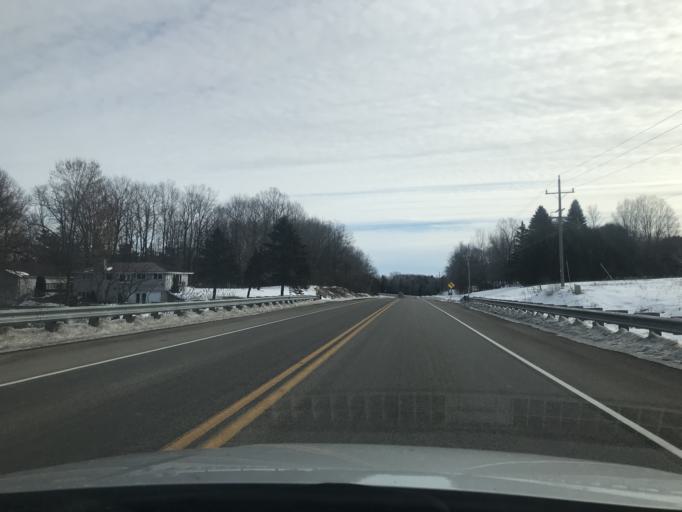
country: US
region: Wisconsin
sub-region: Oconto County
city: Oconto Falls
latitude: 44.8903
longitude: -88.1676
